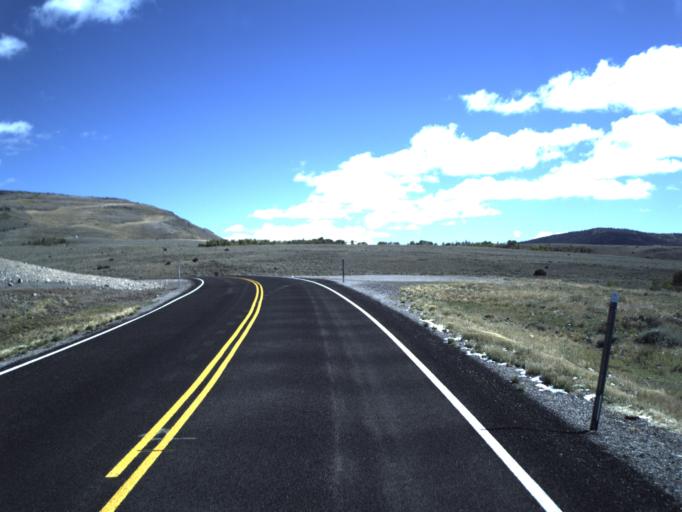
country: US
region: Utah
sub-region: Wayne County
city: Loa
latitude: 38.4999
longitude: -111.8012
